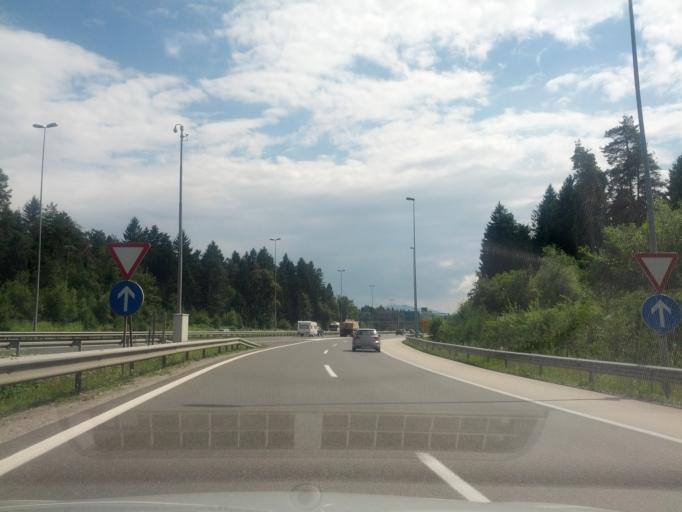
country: SI
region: Ljubljana
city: Ljubljana
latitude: 46.0663
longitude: 14.4565
